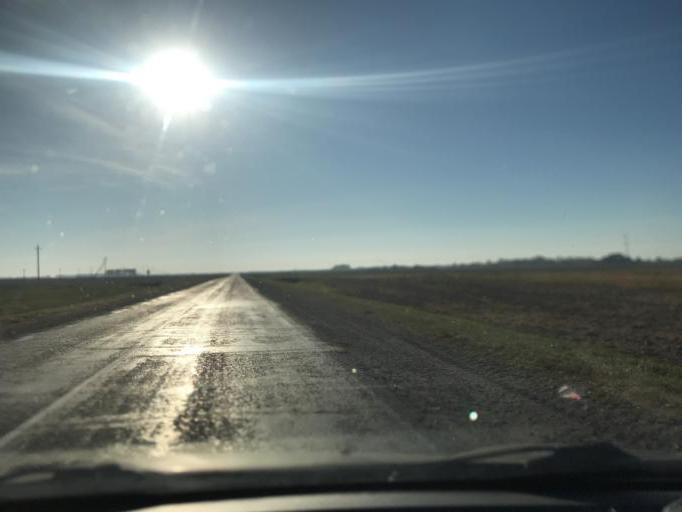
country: BY
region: Gomel
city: Khoyniki
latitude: 51.8456
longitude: 30.0294
